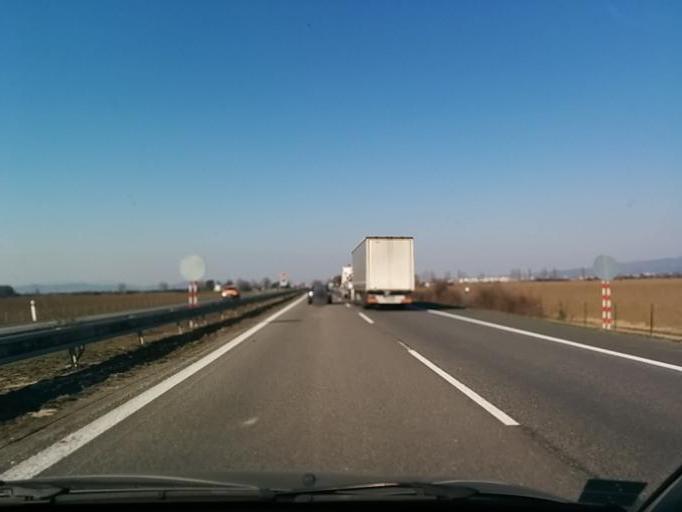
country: SK
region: Trnavsky
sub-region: Okres Trnava
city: Piestany
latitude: 48.5470
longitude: 17.7873
